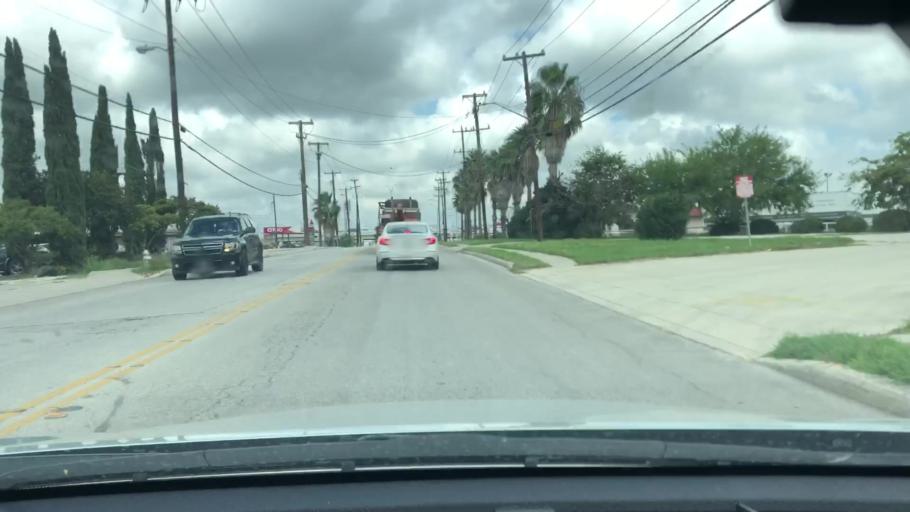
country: US
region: Texas
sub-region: Bexar County
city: Windcrest
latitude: 29.5375
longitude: -98.3792
